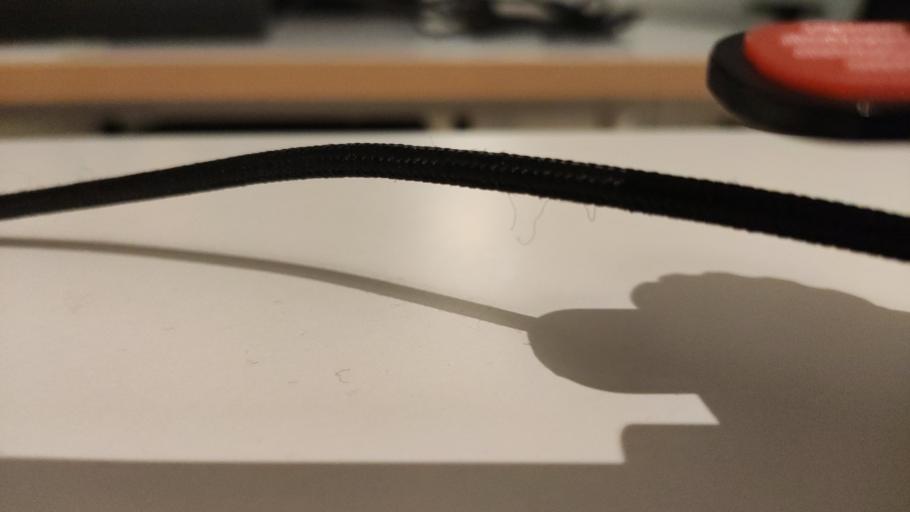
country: RU
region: Moskovskaya
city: Rogachevo
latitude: 56.4356
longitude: 37.1807
